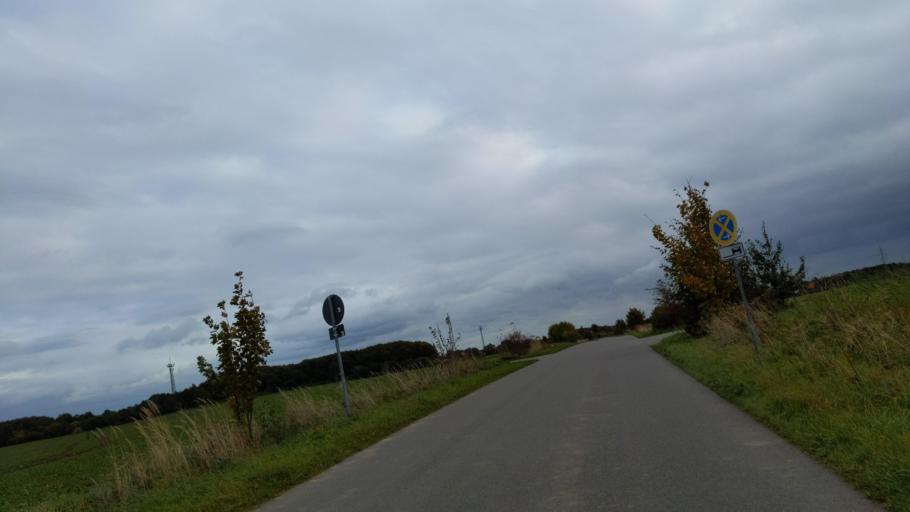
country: DE
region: Schleswig-Holstein
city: Sierksdorf
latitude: 54.0701
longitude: 10.7440
